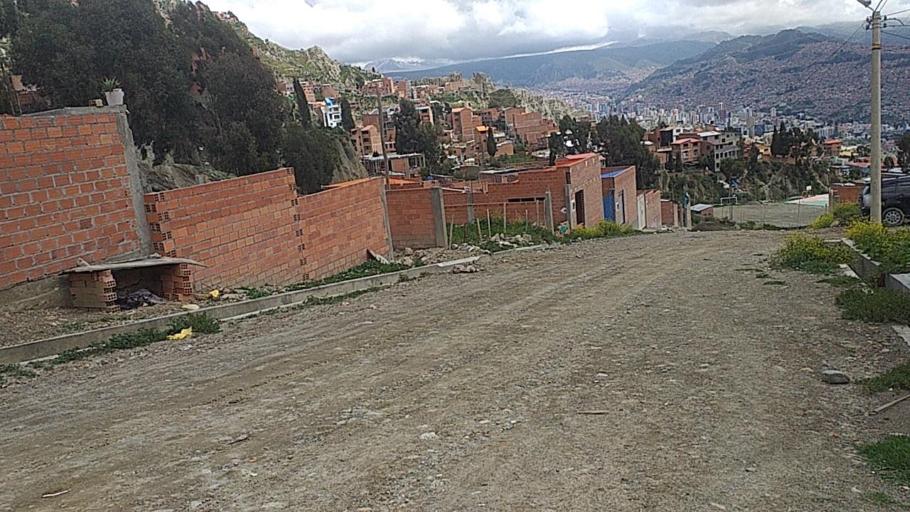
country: BO
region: La Paz
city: La Paz
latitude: -16.5370
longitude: -68.1379
